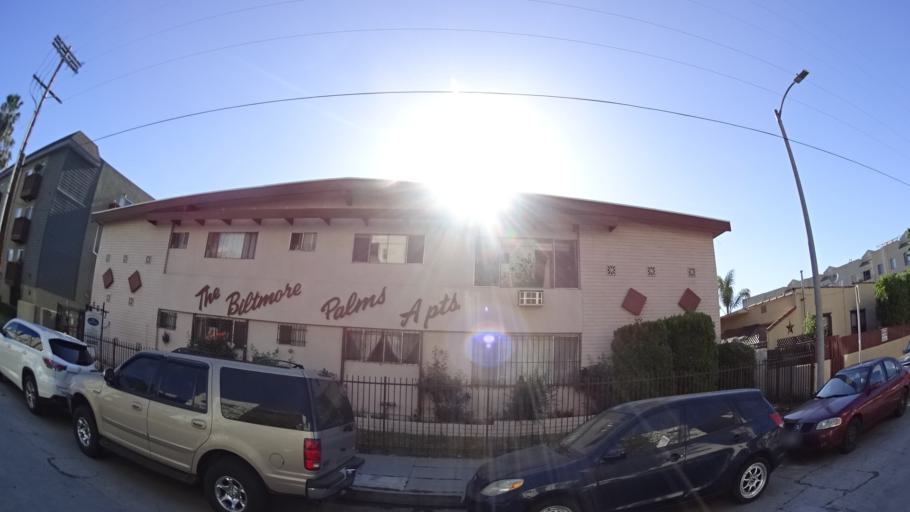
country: US
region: California
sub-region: Los Angeles County
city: North Hollywood
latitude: 34.1612
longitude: -118.3775
